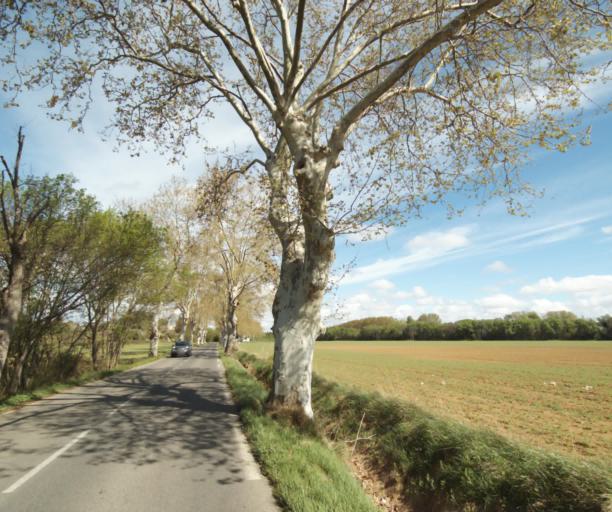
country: FR
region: Languedoc-Roussillon
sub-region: Departement de l'Herault
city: Villeneuve-les-Maguelone
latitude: 43.5479
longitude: 3.8469
